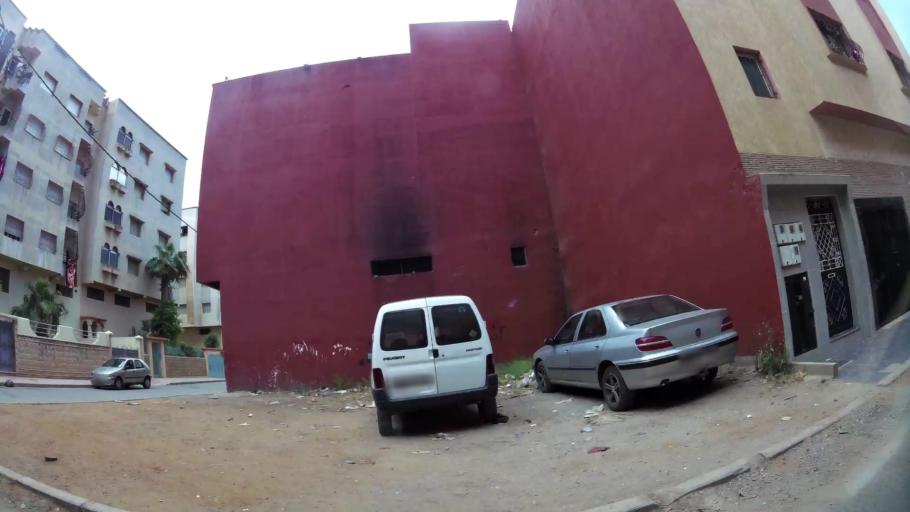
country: MA
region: Rabat-Sale-Zemmour-Zaer
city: Sale
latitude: 34.0612
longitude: -6.7841
